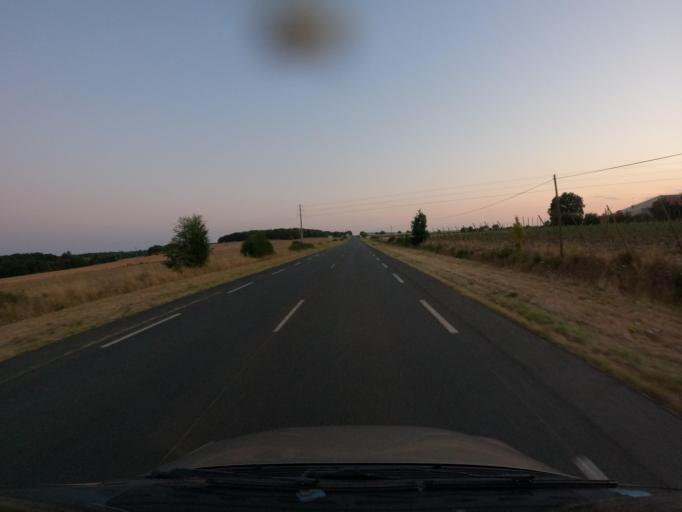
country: FR
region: Pays de la Loire
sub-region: Departement de Maine-et-Loire
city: Cande
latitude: 47.5523
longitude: -1.0526
